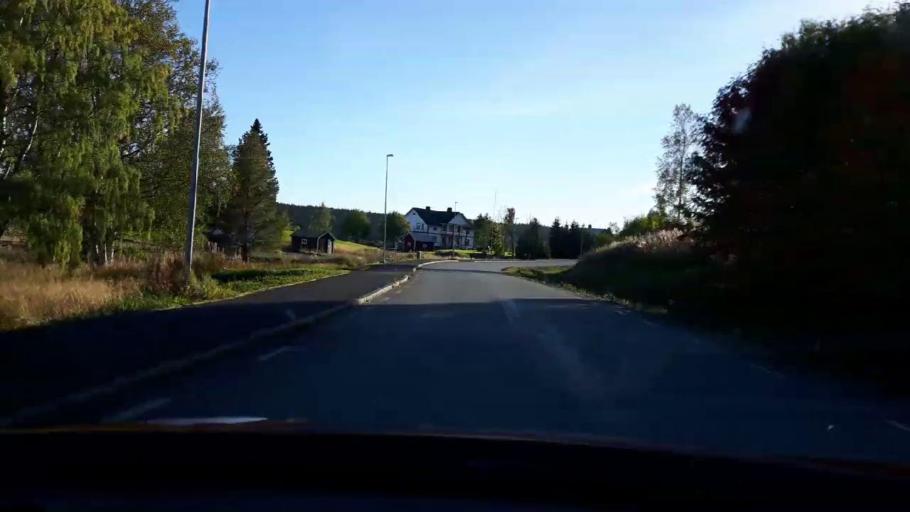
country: SE
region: Jaemtland
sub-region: OEstersunds Kommun
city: Lit
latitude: 63.8124
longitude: 14.7958
